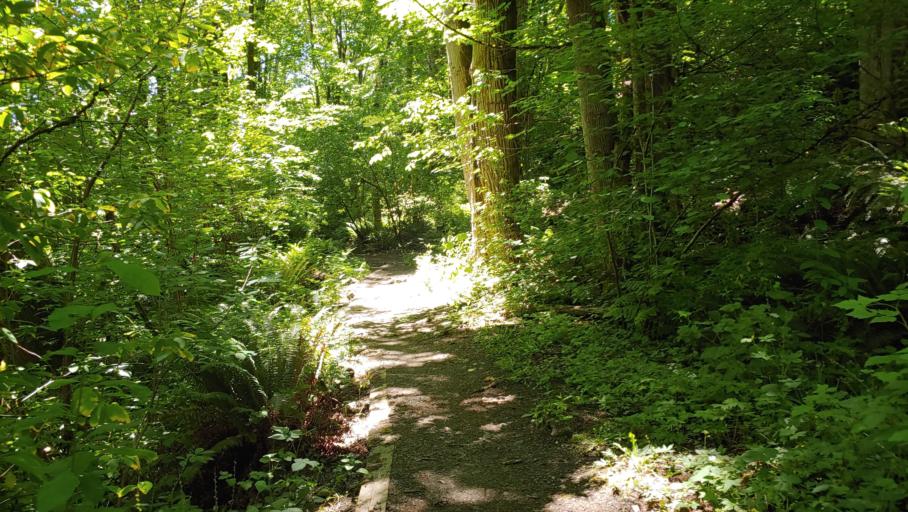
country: US
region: Washington
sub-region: King County
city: Newcastle
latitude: 47.5192
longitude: -122.1788
